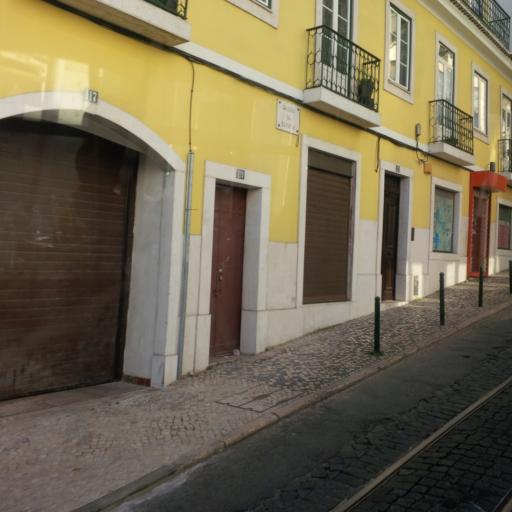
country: PT
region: Lisbon
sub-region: Lisbon
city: Lisbon
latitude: 38.7126
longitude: -9.1568
